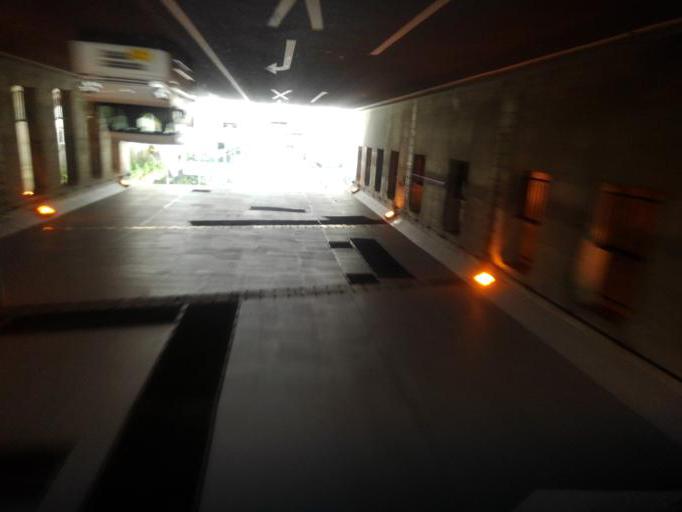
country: JP
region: Tokyo
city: Hino
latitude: 35.6981
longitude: 139.4184
